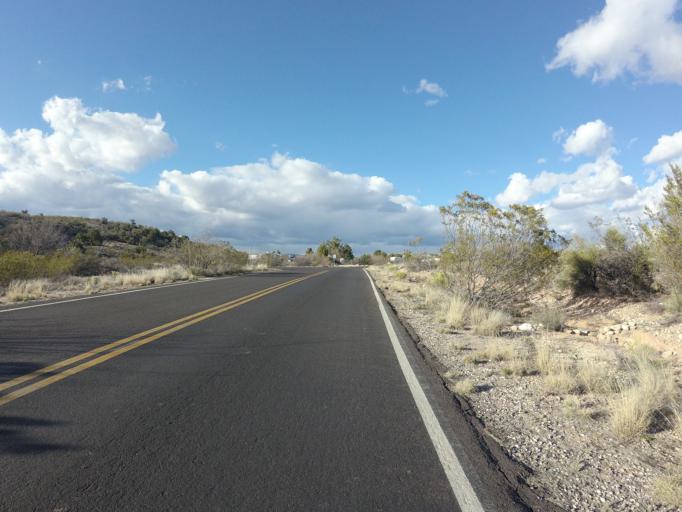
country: US
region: Arizona
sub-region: Yavapai County
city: Cottonwood
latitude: 34.7573
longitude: -112.0154
